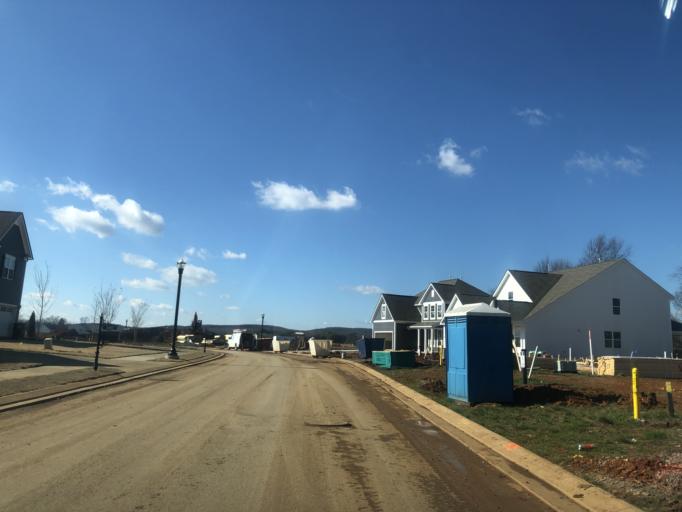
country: US
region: Tennessee
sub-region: Rutherford County
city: Smyrna
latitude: 35.8868
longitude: -86.4878
